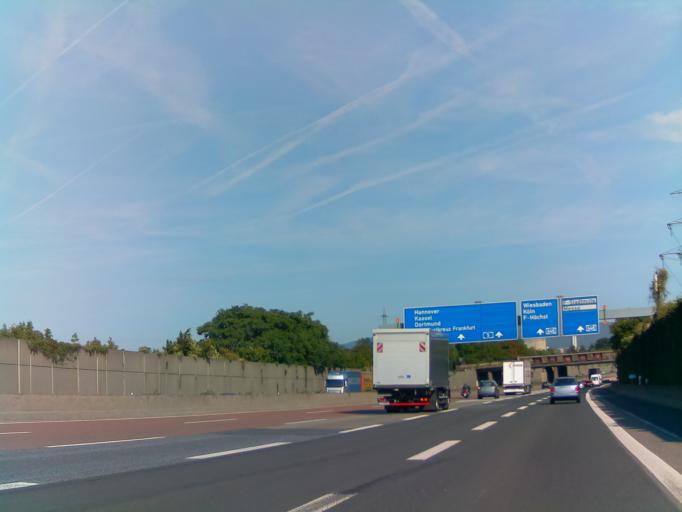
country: DE
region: Hesse
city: Niederrad
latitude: 50.1043
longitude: 8.6083
